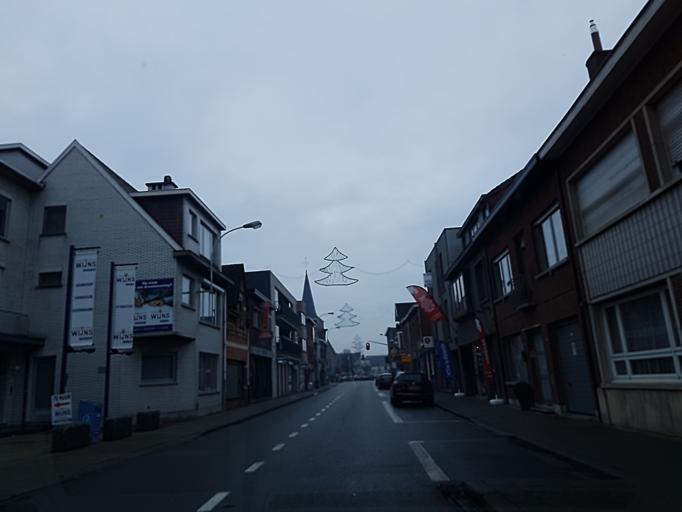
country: BE
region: Flanders
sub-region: Provincie Antwerpen
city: Nijlen
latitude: 51.1619
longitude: 4.6688
